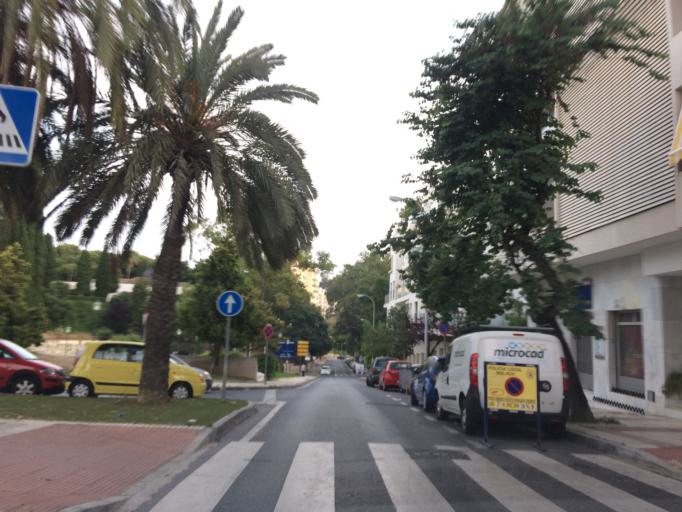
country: ES
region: Andalusia
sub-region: Provincia de Malaga
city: Malaga
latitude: 36.7298
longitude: -4.4028
